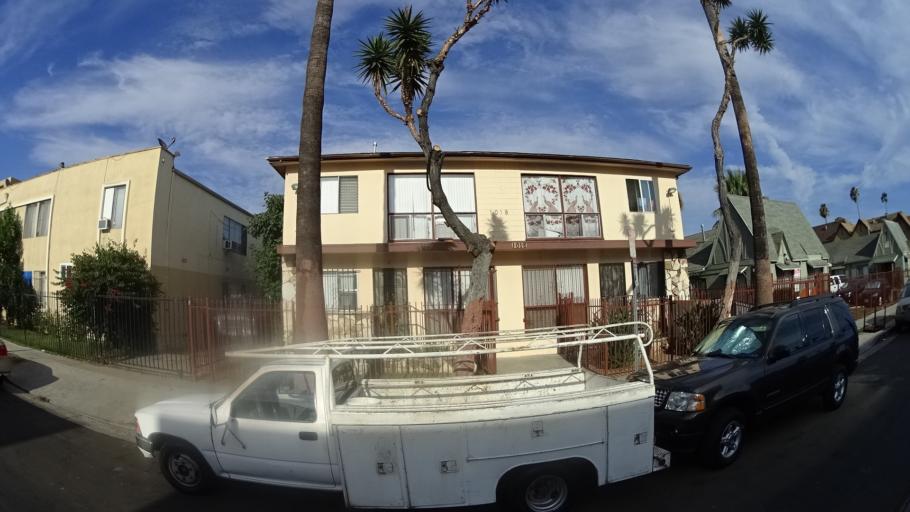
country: US
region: California
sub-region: Los Angeles County
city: Hollywood
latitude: 34.0897
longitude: -118.2992
